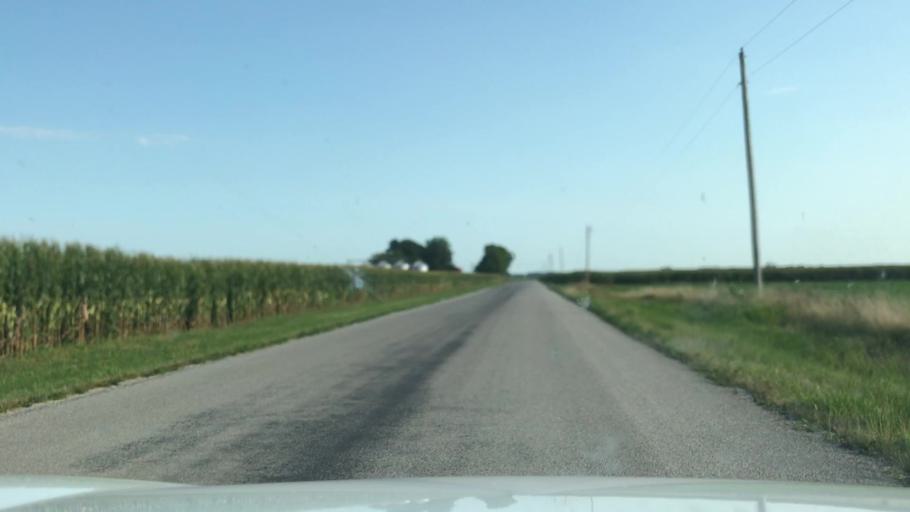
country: US
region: Illinois
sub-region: Washington County
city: Okawville
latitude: 38.4212
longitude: -89.4777
